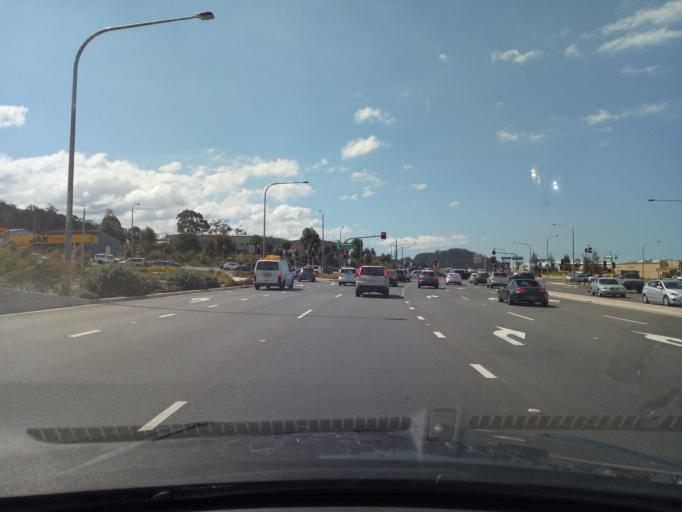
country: AU
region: New South Wales
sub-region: Gosford Shire
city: Point Clare
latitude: -33.4280
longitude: 151.3171
